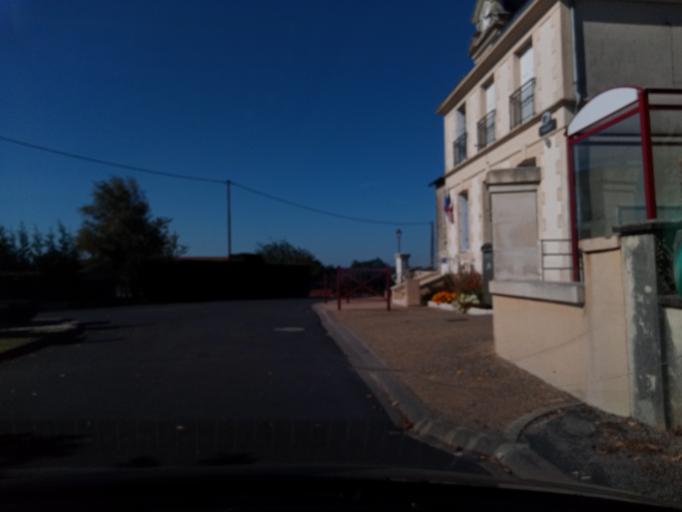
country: FR
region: Poitou-Charentes
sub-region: Departement de la Vienne
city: Saint-Savin
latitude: 46.5074
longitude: 0.7754
